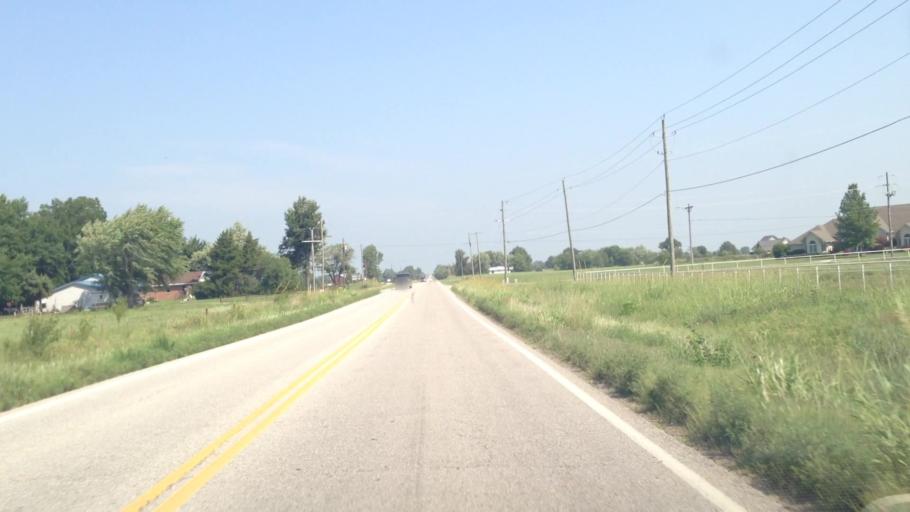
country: US
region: Oklahoma
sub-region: Craig County
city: Vinita
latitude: 36.6693
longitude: -95.1436
